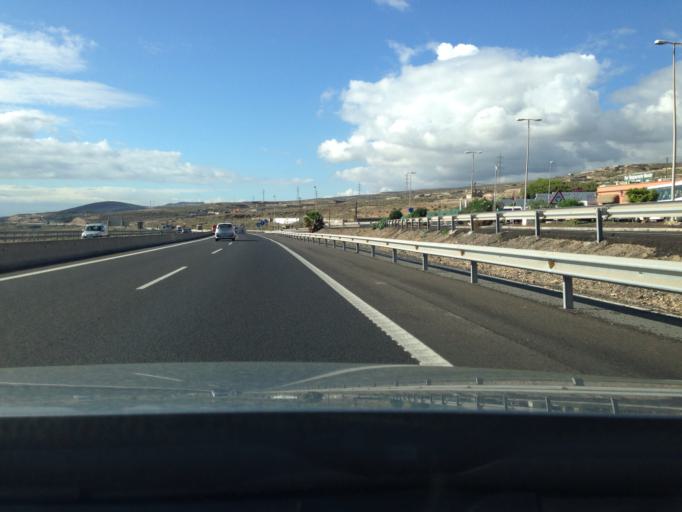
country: ES
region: Canary Islands
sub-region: Provincia de Santa Cruz de Tenerife
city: Fasnia
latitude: 28.2138
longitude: -16.4225
